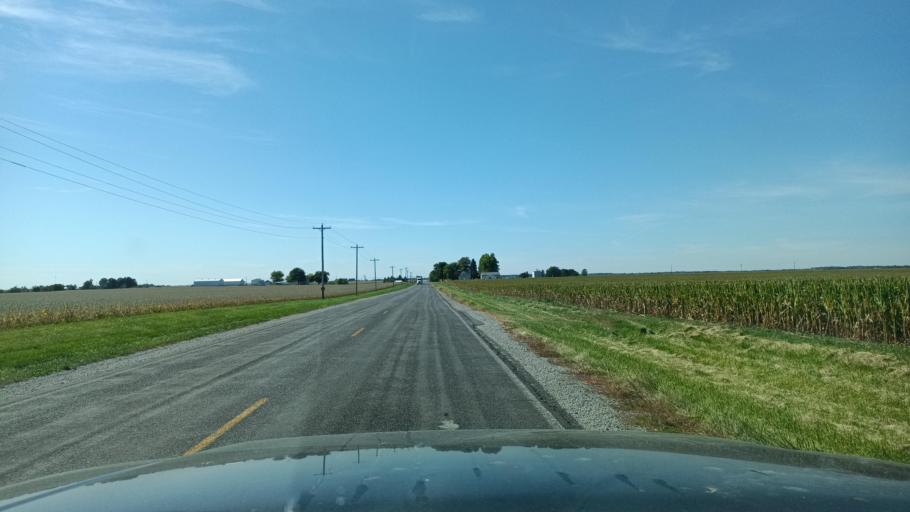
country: US
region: Illinois
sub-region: De Witt County
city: Farmer City
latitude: 40.2239
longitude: -88.7306
